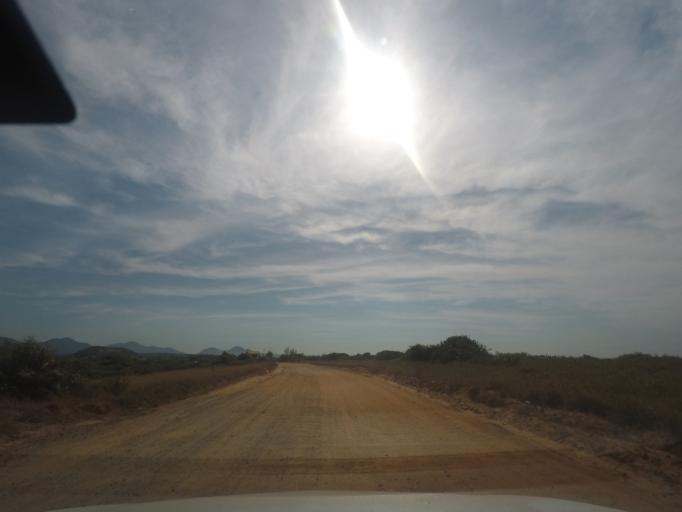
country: BR
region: Rio de Janeiro
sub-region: Marica
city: Marica
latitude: -22.9605
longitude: -42.8409
